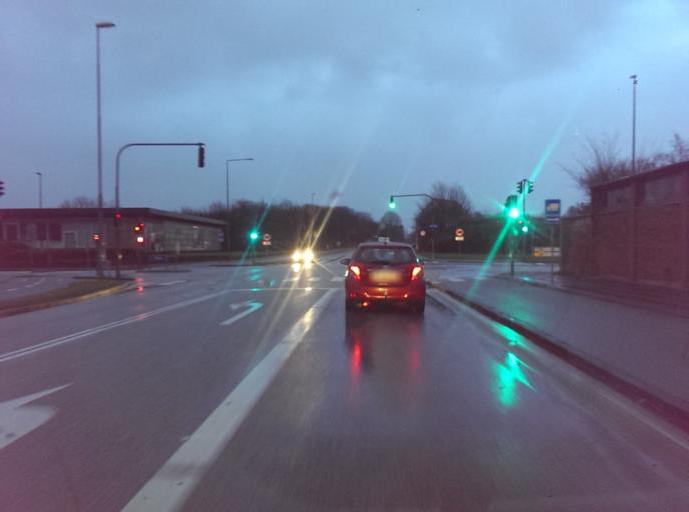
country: DK
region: South Denmark
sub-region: Esbjerg Kommune
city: Esbjerg
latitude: 55.4634
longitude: 8.4641
